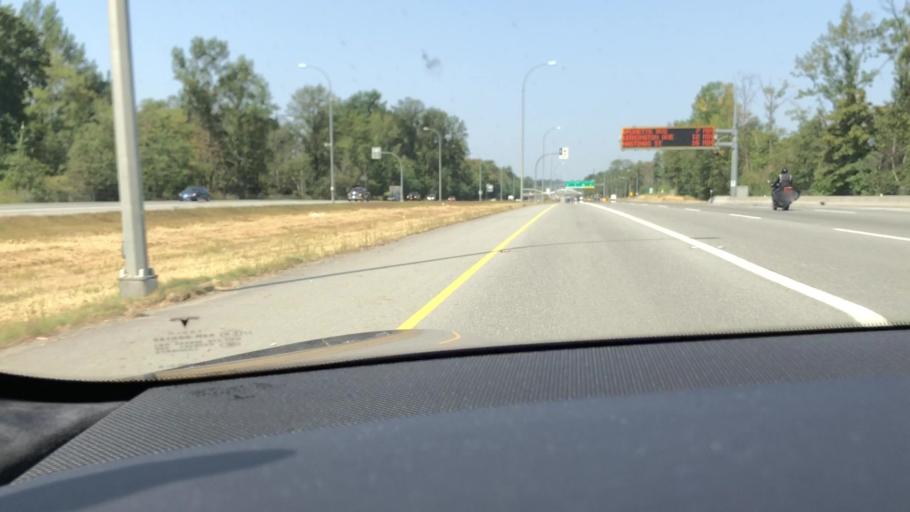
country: CA
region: British Columbia
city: Pitt Meadows
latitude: 49.1841
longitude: -122.7446
